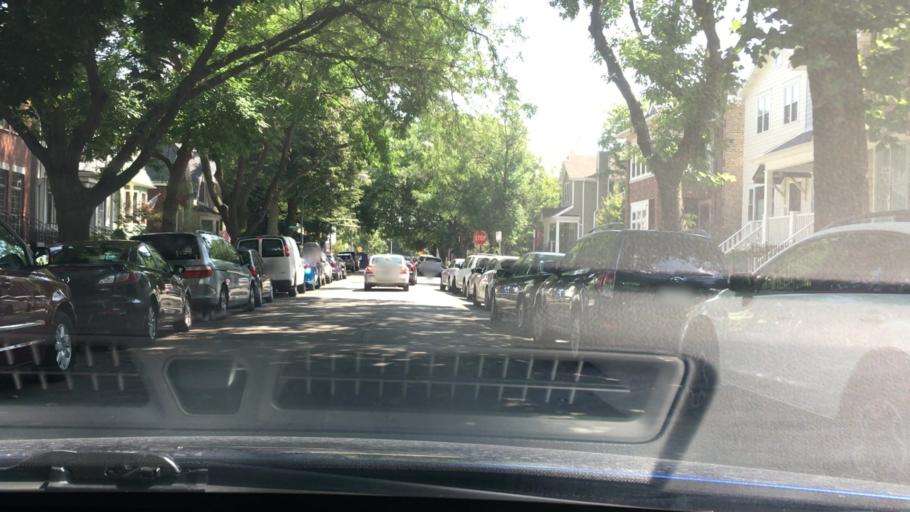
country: US
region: Illinois
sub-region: Cook County
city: Lincolnwood
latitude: 41.9559
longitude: -87.6820
